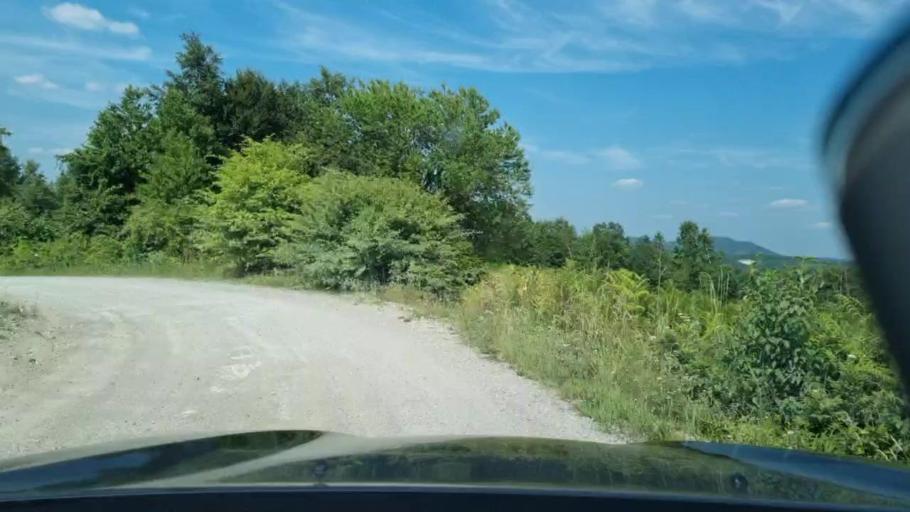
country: BA
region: Federation of Bosnia and Herzegovina
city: Bosanska Krupa
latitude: 44.8193
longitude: 16.1758
